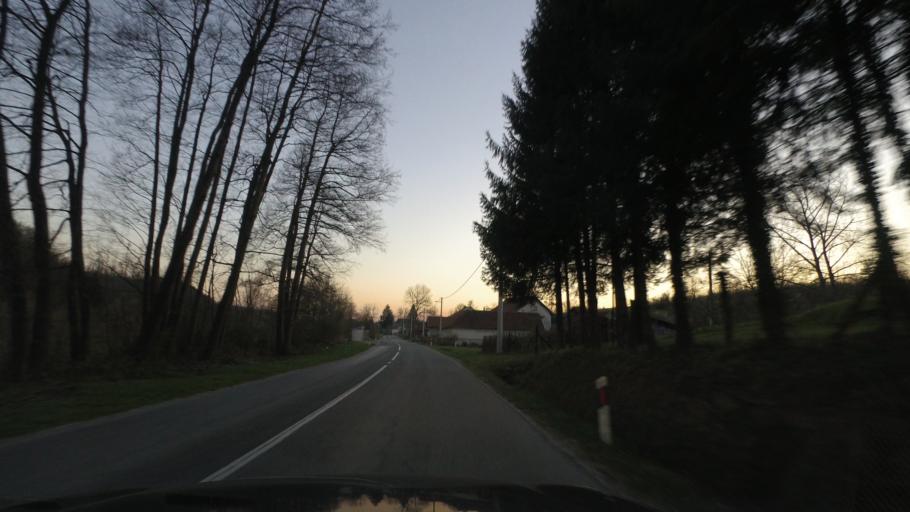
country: HR
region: Karlovacka
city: Vojnic
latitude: 45.3330
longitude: 15.7163
